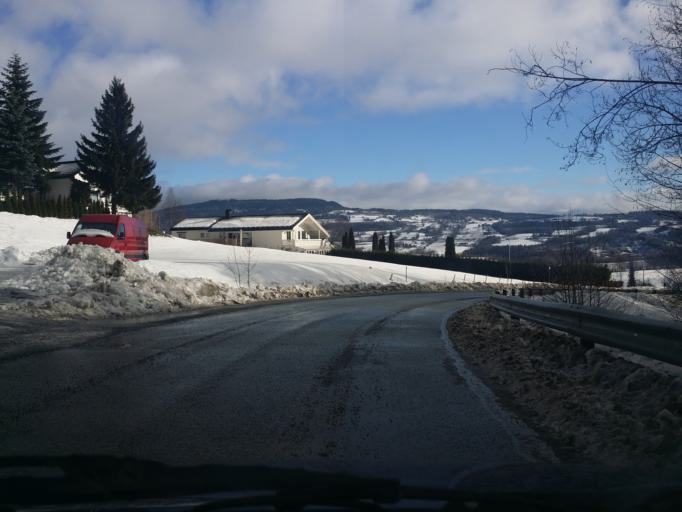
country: NO
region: Buskerud
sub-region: Lier
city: Lierbyen
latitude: 59.8216
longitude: 10.1996
